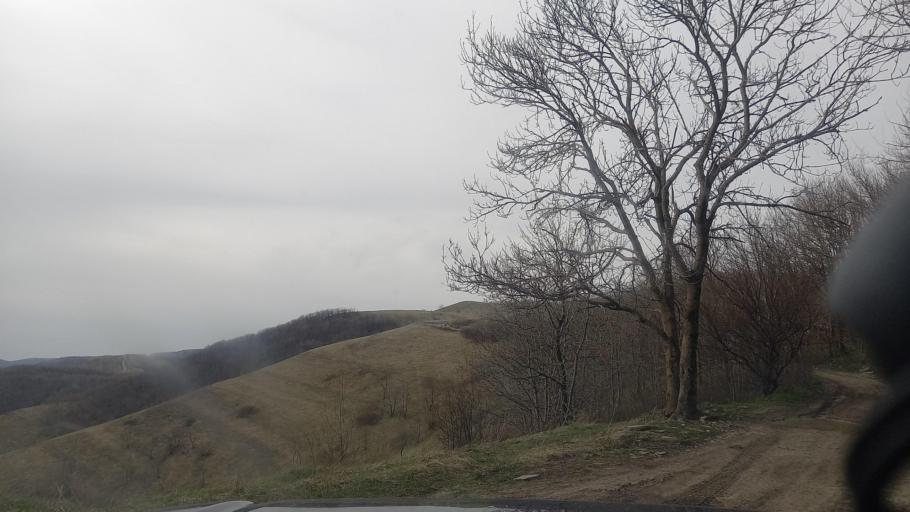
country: RU
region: Krasnodarskiy
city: Divnomorskoye
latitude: 44.6141
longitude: 38.2220
